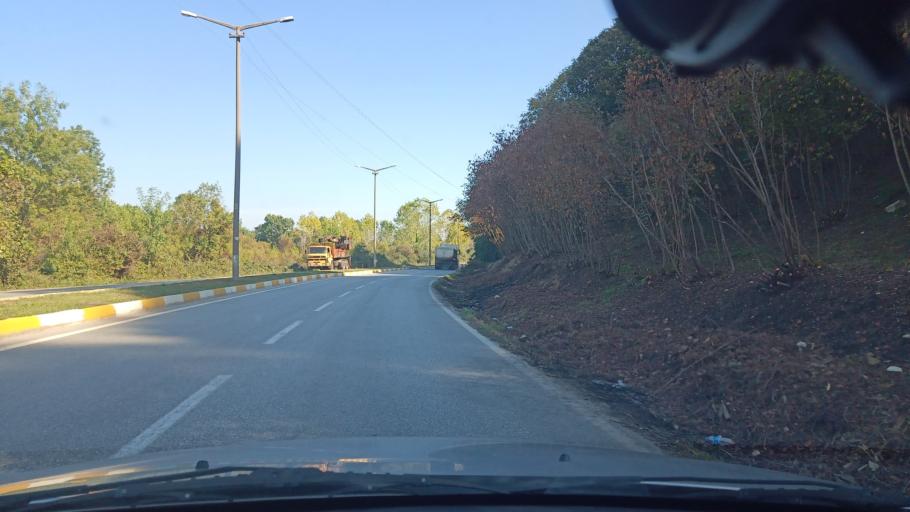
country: TR
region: Sakarya
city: Karasu
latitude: 41.1014
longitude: 30.6601
